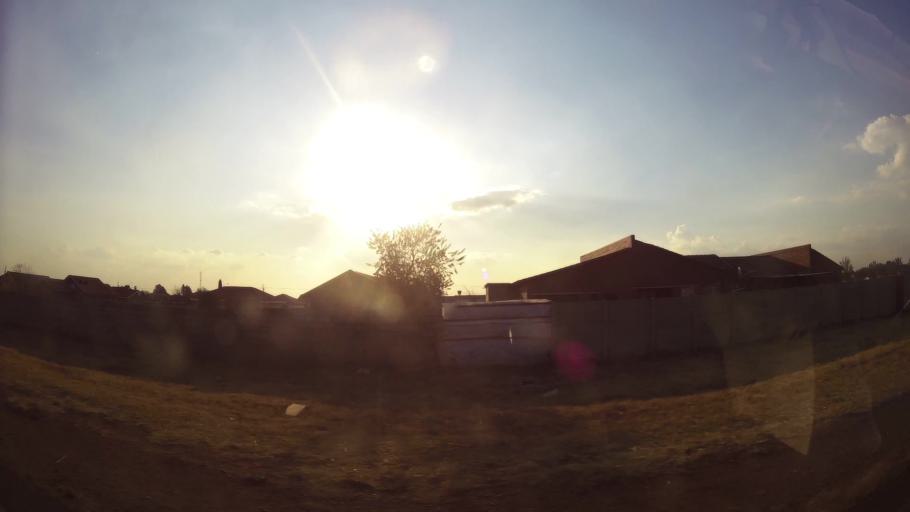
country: ZA
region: Gauteng
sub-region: Ekurhuleni Metropolitan Municipality
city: Boksburg
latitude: -26.3155
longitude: 28.2526
